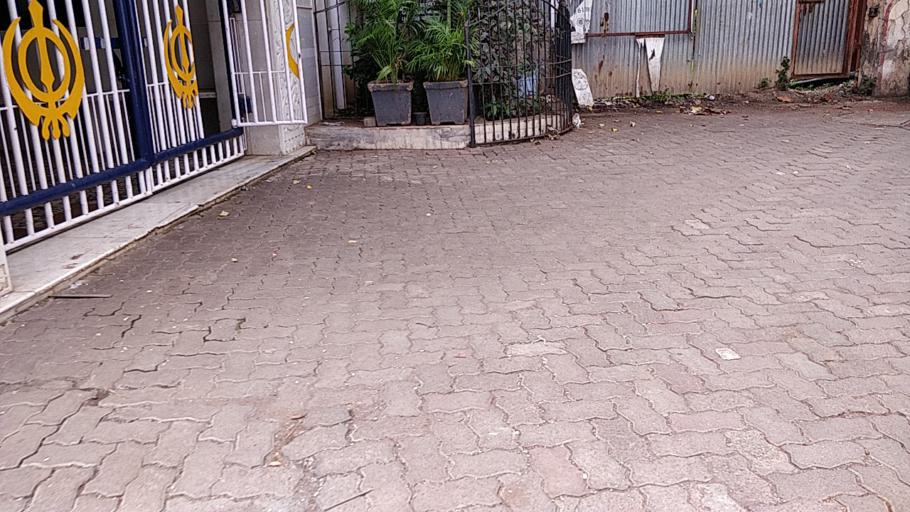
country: IN
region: Maharashtra
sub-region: Mumbai Suburban
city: Mumbai
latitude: 19.0774
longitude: 72.8611
